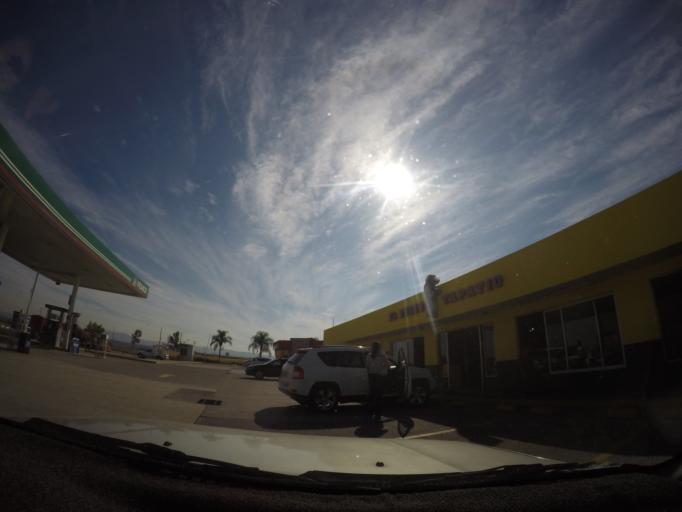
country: MX
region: Puebla
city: Necaxa
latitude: 20.2291
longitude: -98.0297
